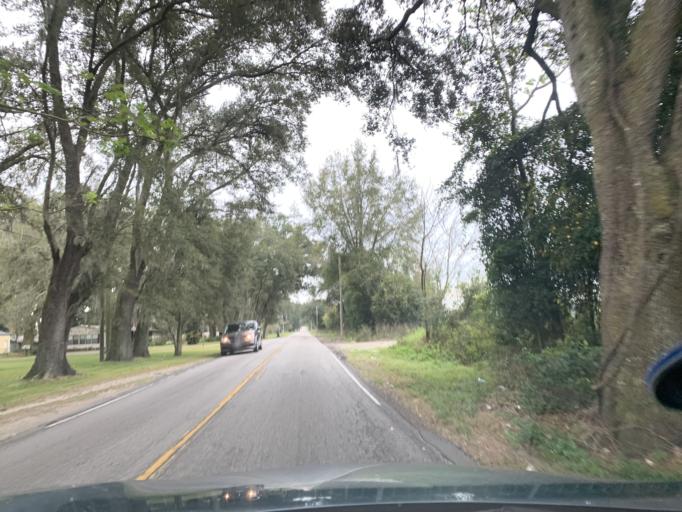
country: US
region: Florida
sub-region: Pasco County
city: Zephyrhills North
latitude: 28.2830
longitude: -82.1797
